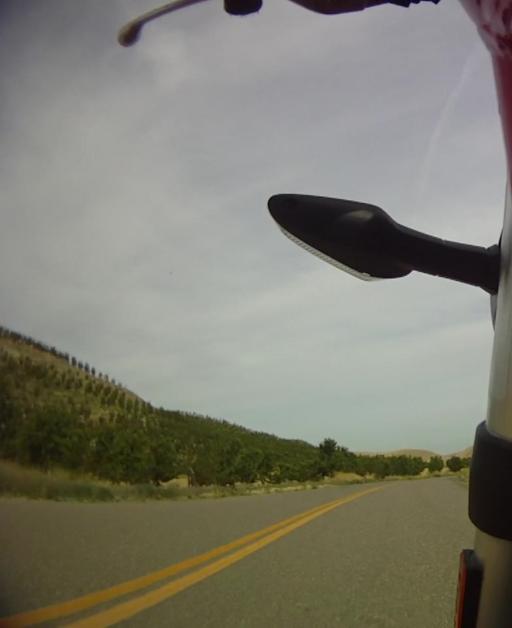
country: US
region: California
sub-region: Stanislaus County
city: Patterson
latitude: 37.4737
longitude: -121.2021
